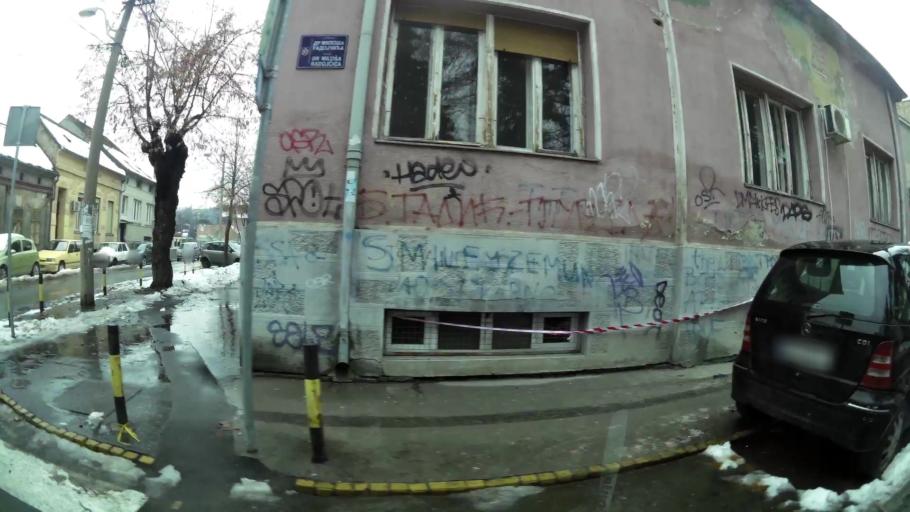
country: RS
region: Central Serbia
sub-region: Belgrade
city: Zemun
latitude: 44.8421
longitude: 20.4085
